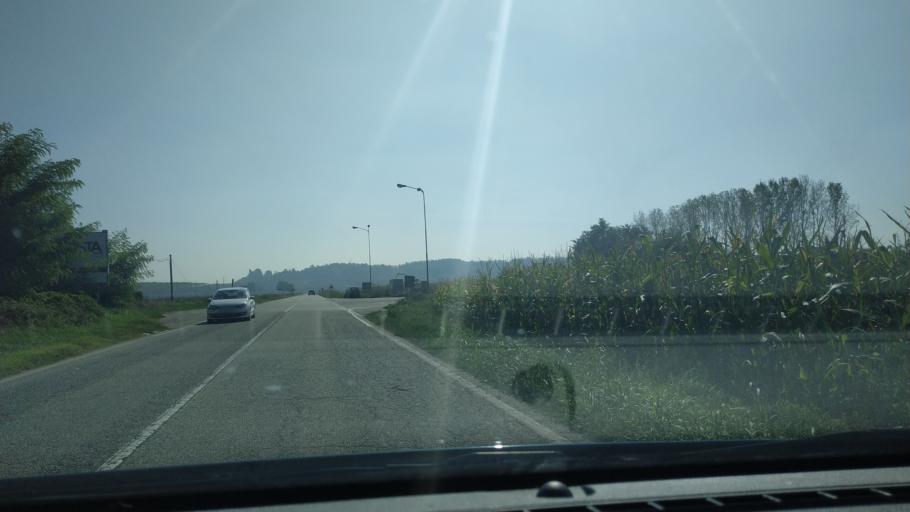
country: IT
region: Piedmont
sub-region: Provincia di Alessandria
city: Giarole
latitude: 45.0745
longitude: 8.5745
